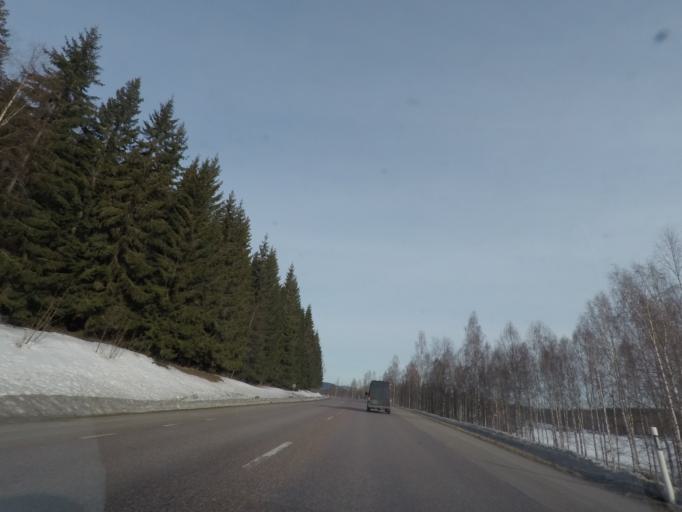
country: SE
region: Dalarna
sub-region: Smedjebackens Kommun
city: Smedjebacken
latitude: 60.1225
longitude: 15.4725
